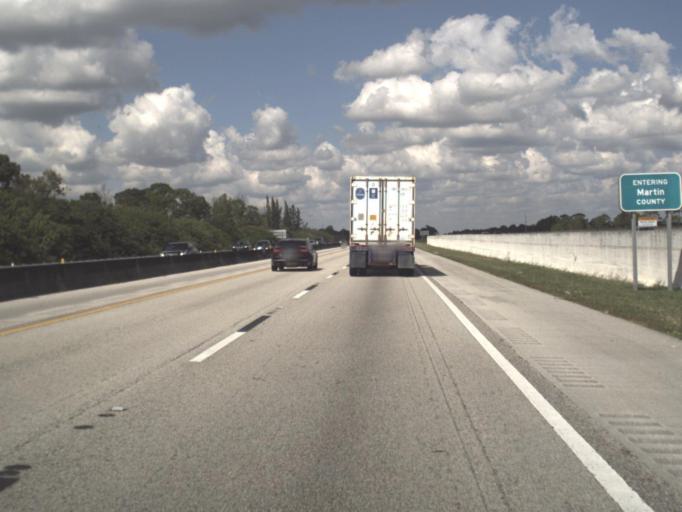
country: US
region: Florida
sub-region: Palm Beach County
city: Limestone Creek
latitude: 26.9569
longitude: -80.1673
